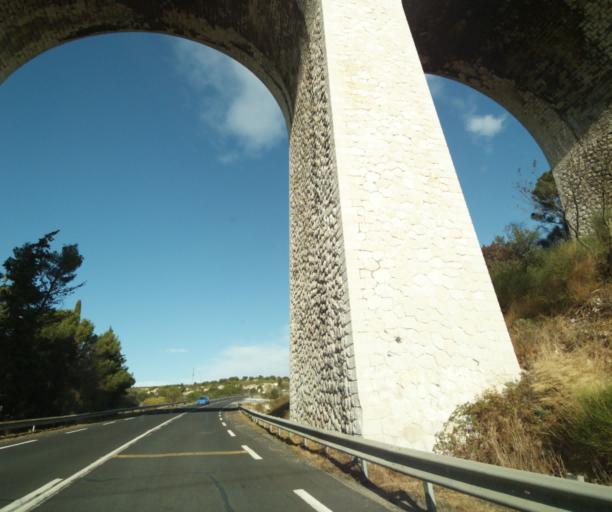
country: FR
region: Provence-Alpes-Cote d'Azur
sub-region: Departement des Bouches-du-Rhone
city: Sausset-les-Pins
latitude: 43.3399
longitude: 5.0487
